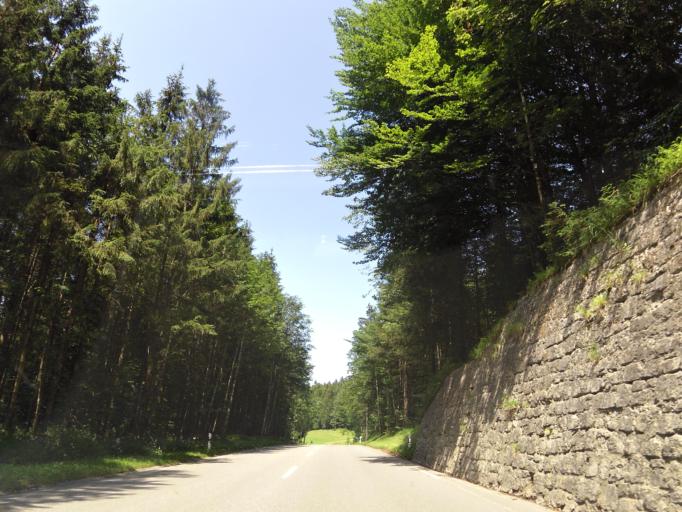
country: DE
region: Bavaria
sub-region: Upper Bavaria
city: Inzell
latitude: 47.7471
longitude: 12.7300
